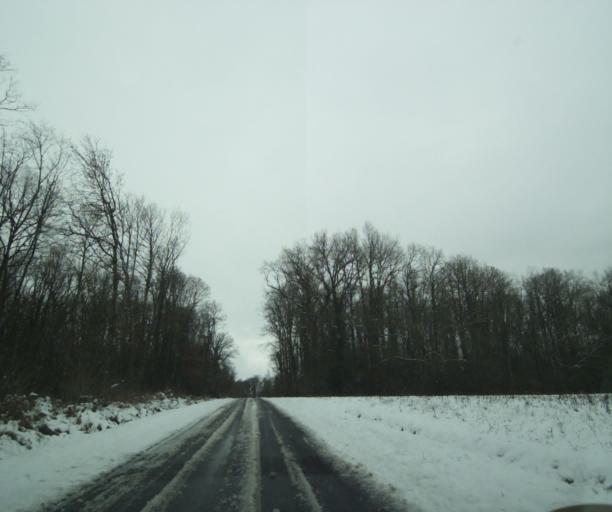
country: FR
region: Champagne-Ardenne
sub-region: Departement de la Haute-Marne
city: Montier-en-Der
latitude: 48.4236
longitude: 4.7279
